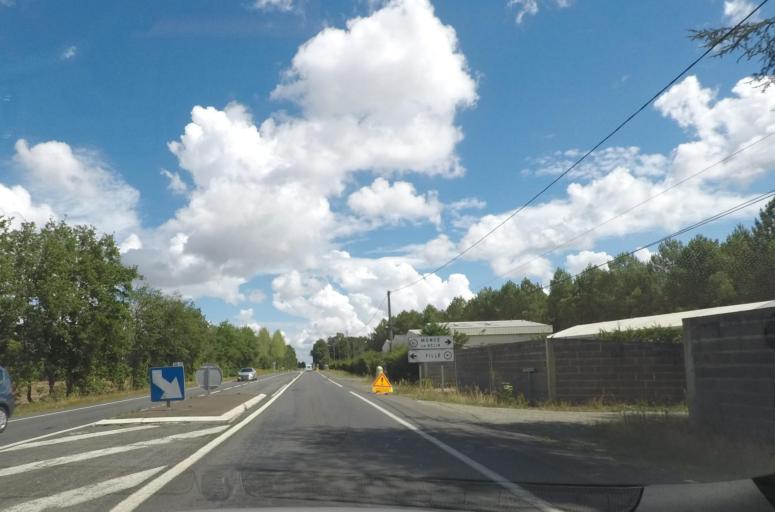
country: FR
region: Pays de la Loire
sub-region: Departement de la Sarthe
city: Guecelard
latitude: 47.8900
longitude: 0.1454
